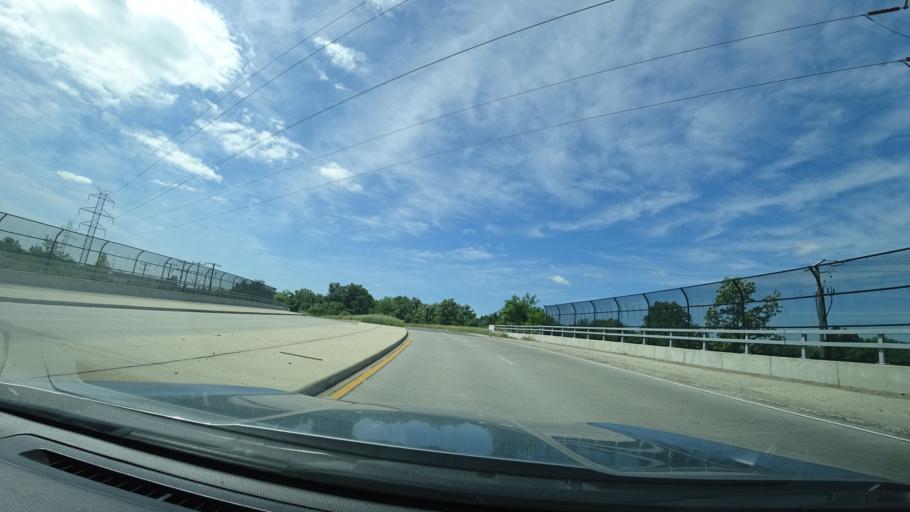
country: US
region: Virginia
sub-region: Loudoun County
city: Sterling
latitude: 39.0092
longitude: -77.4305
